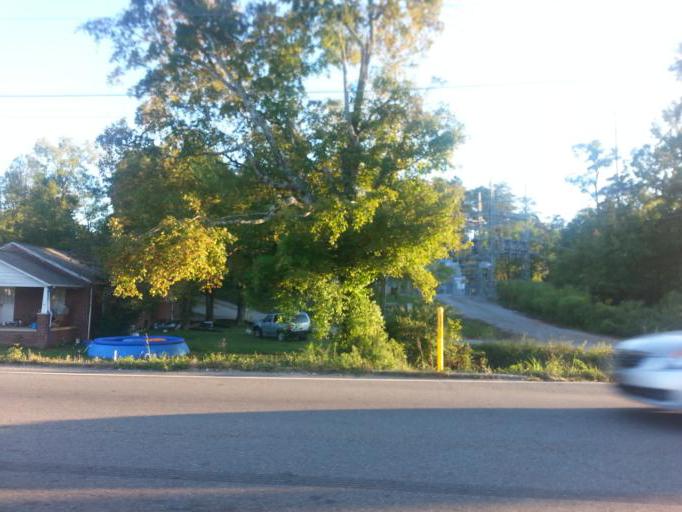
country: US
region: Tennessee
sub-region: Sevier County
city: Seymour
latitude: 35.9008
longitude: -83.8219
